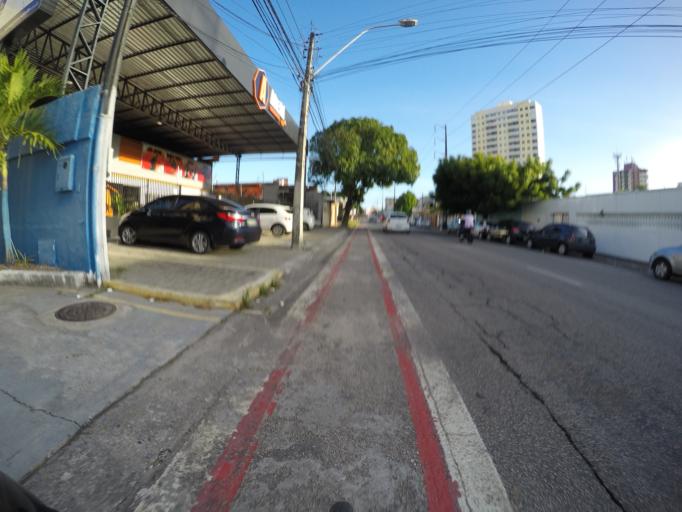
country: BR
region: Ceara
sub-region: Fortaleza
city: Fortaleza
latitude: -3.7476
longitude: -38.5131
